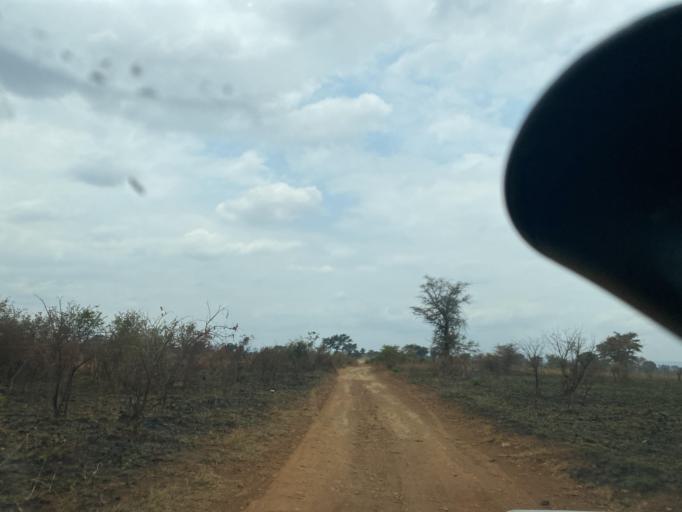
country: ZM
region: Lusaka
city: Chongwe
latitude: -15.4950
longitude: 28.7985
